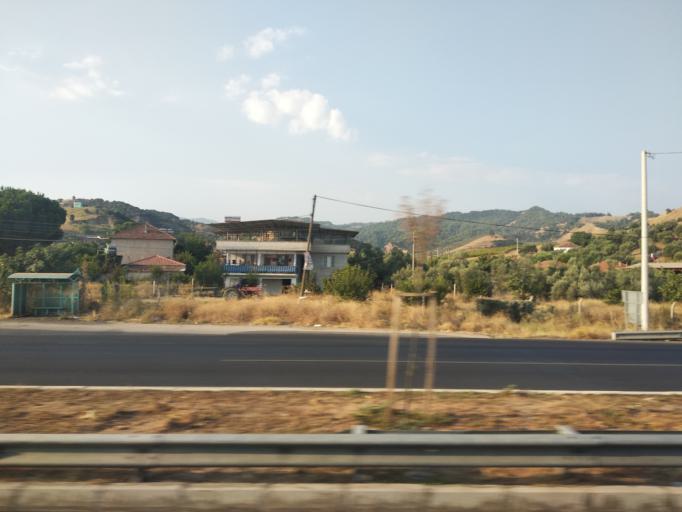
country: TR
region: Manisa
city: Ahmetli
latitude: 38.5096
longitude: 27.9789
